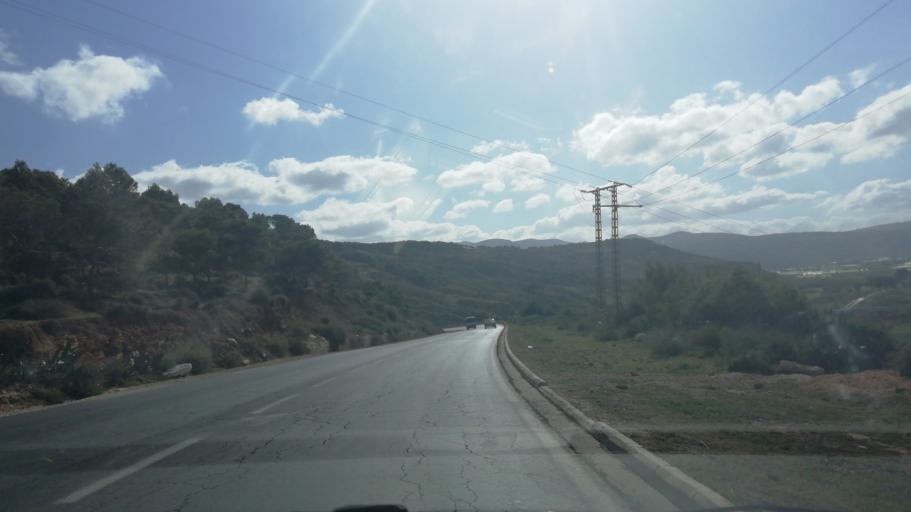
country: DZ
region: Relizane
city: Mazouna
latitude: 36.3085
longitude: 0.6683
